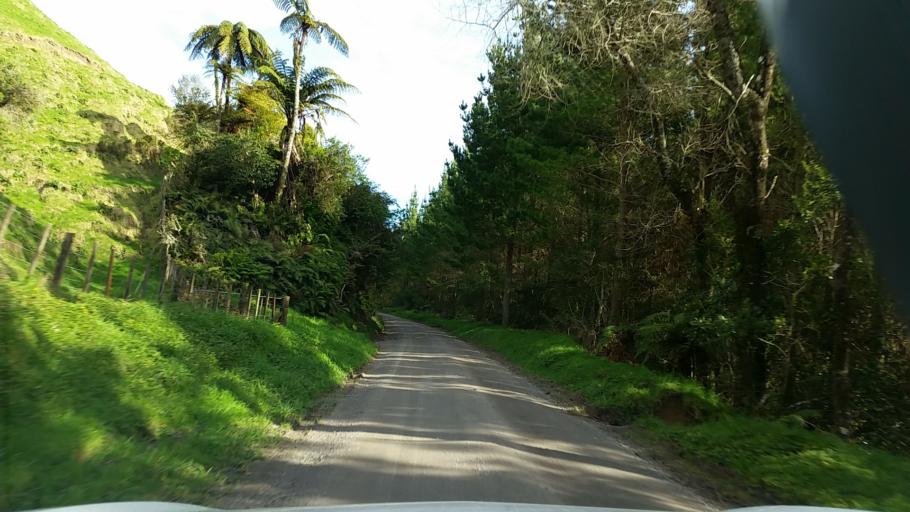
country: NZ
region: Bay of Plenty
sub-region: Rotorua District
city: Rotorua
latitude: -38.2384
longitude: 176.3516
